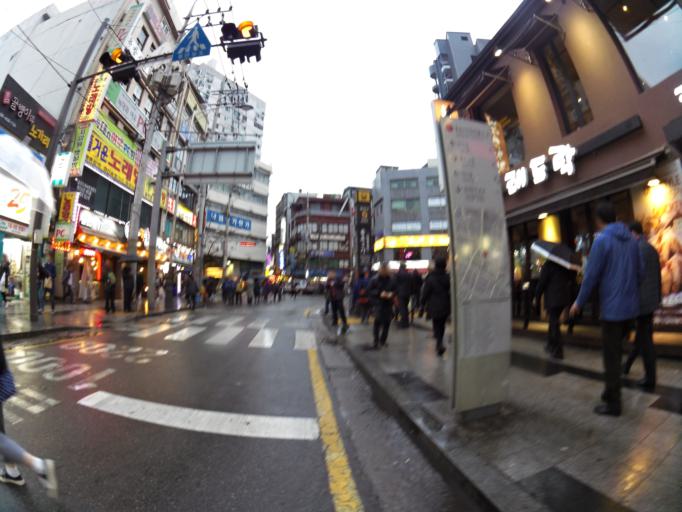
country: KR
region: Seoul
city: Seoul
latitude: 37.5721
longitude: 126.9888
